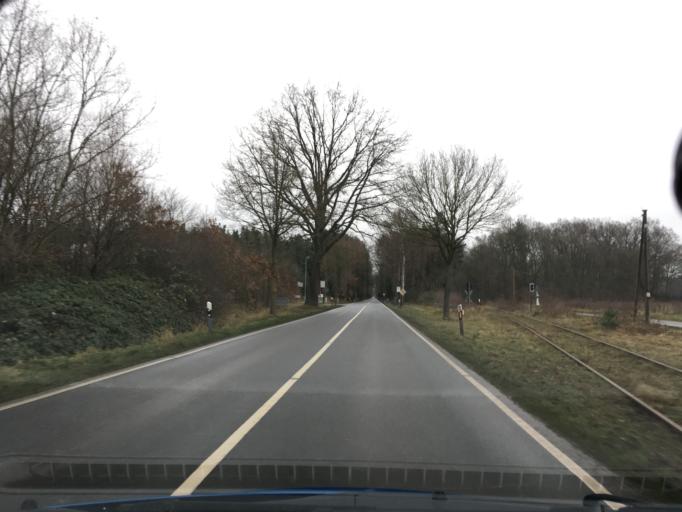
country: DE
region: Lower Saxony
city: Neetze
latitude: 53.2802
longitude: 10.6394
